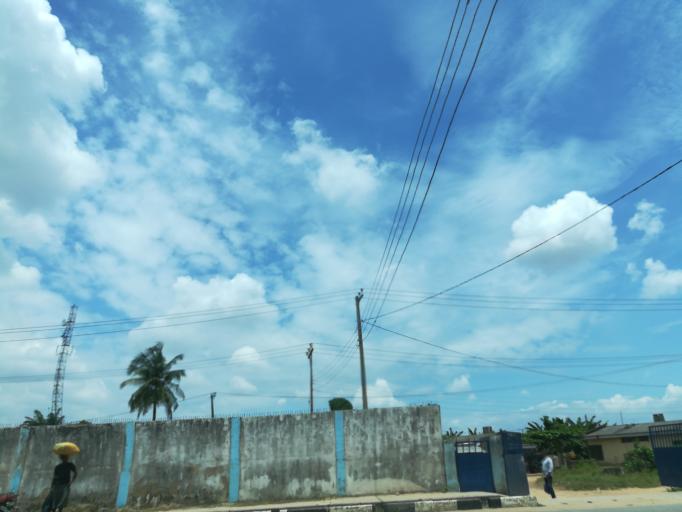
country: NG
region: Lagos
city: Ebute Ikorodu
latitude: 6.5996
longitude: 3.4933
